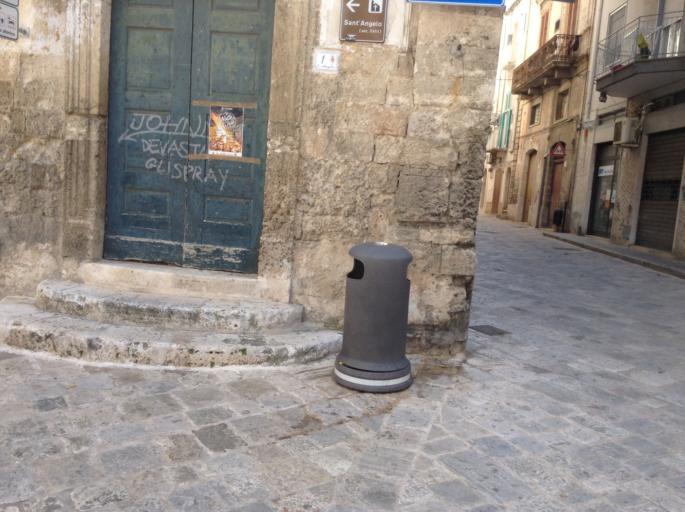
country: IT
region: Apulia
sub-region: Provincia di Bari
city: Monopoli
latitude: 40.9524
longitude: 17.3017
